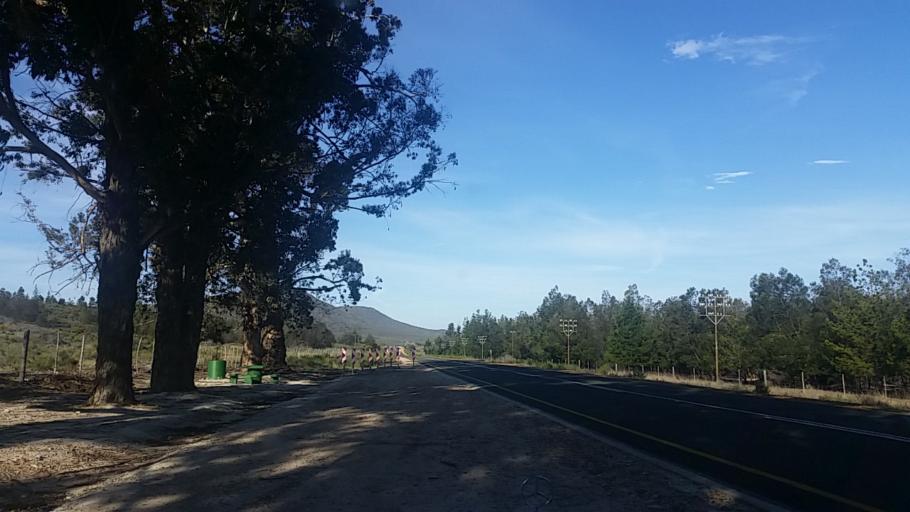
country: ZA
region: Western Cape
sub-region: Eden District Municipality
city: George
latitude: -33.7764
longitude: 22.7025
